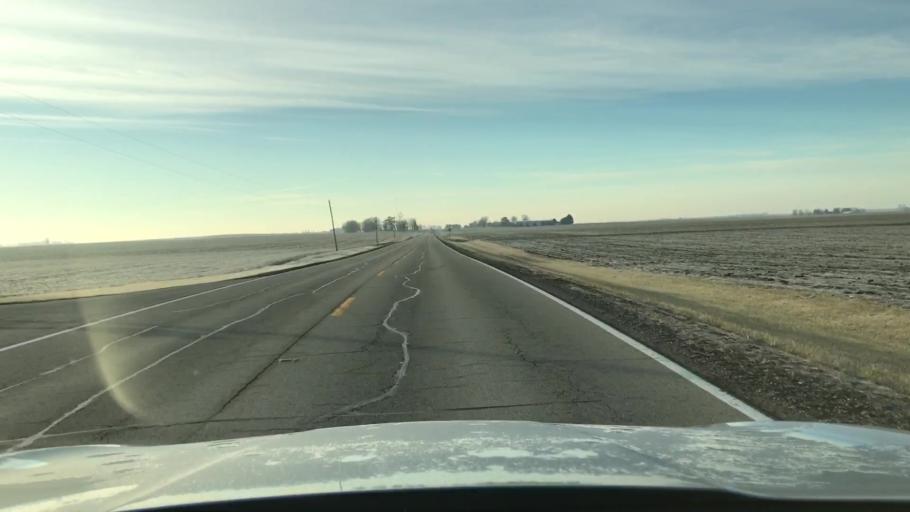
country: US
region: Illinois
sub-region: McLean County
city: Hudson
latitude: 40.6001
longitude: -88.9450
